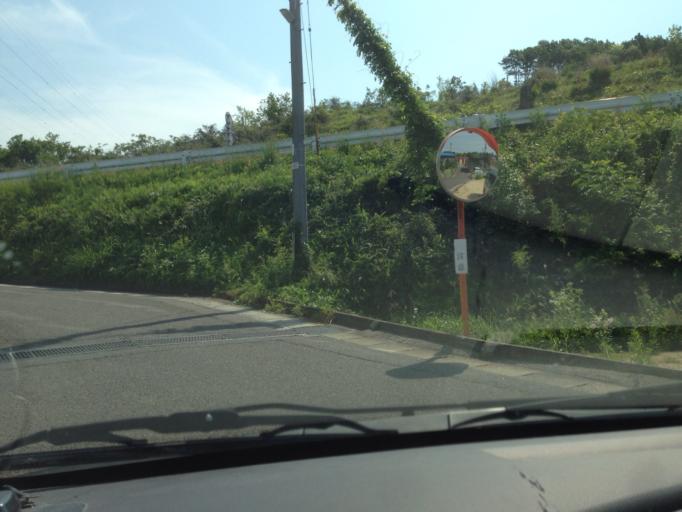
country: JP
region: Fukushima
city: Sukagawa
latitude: 37.1380
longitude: 140.2141
